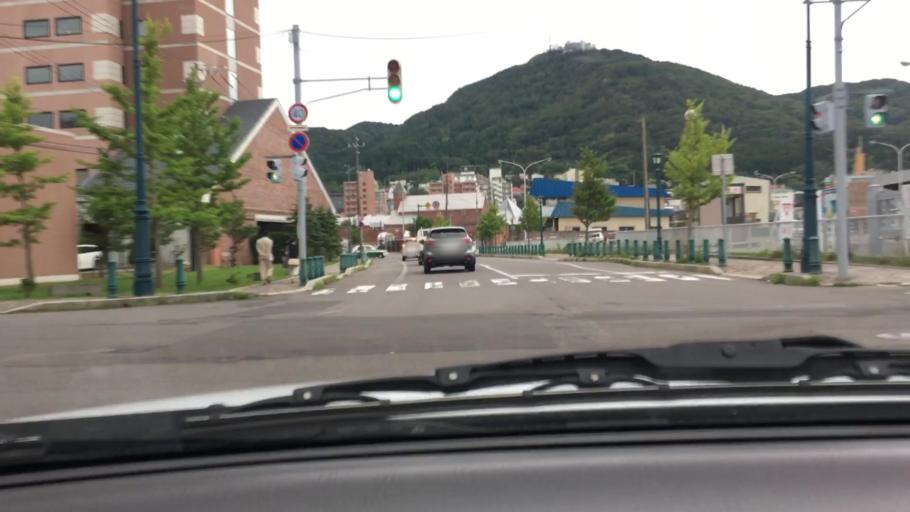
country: JP
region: Hokkaido
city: Hakodate
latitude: 41.7685
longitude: 140.7192
